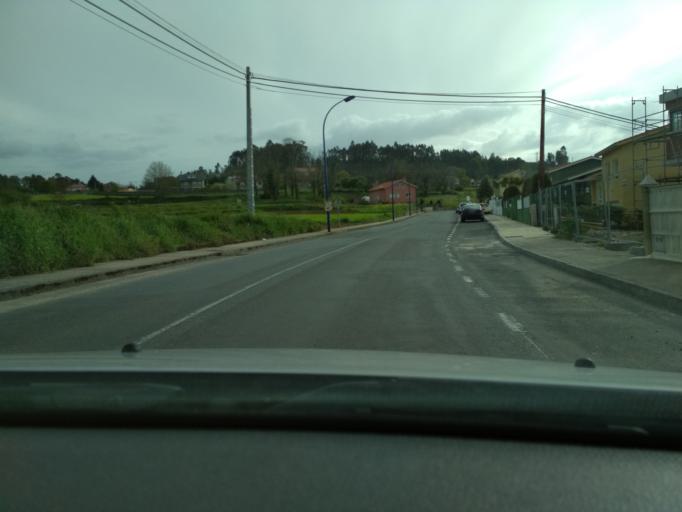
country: ES
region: Galicia
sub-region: Provincia da Coruna
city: Culleredo
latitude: 43.2881
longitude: -8.3819
